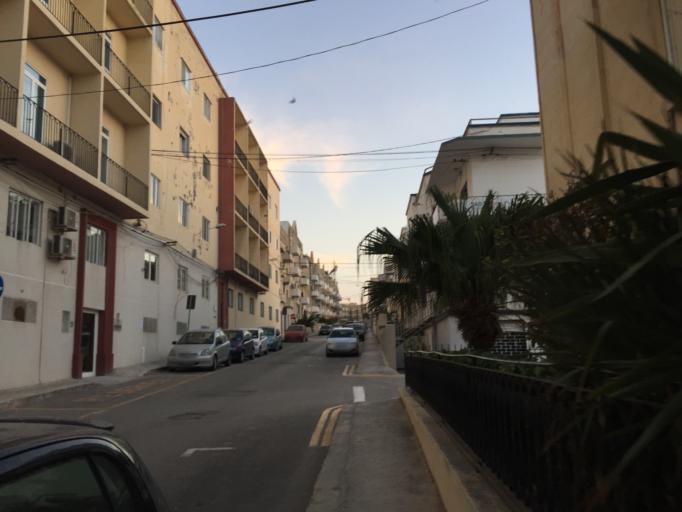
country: MT
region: Ta' Xbiex
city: Ta' Xbiex
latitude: 35.9014
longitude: 14.4944
